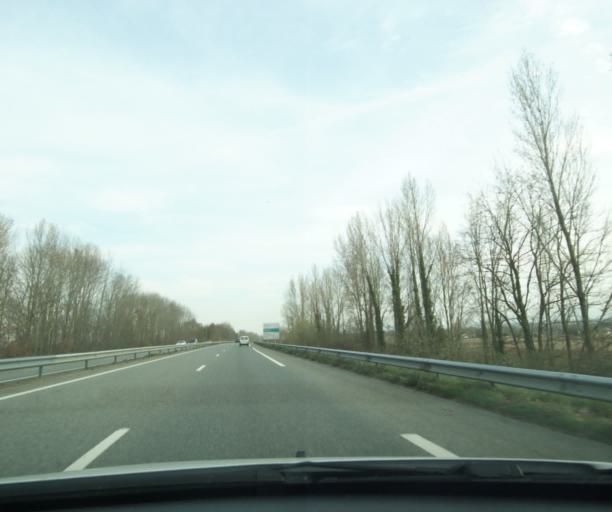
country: FR
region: Midi-Pyrenees
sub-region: Departement des Hautes-Pyrenees
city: Juillan
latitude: 43.2162
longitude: 0.0269
